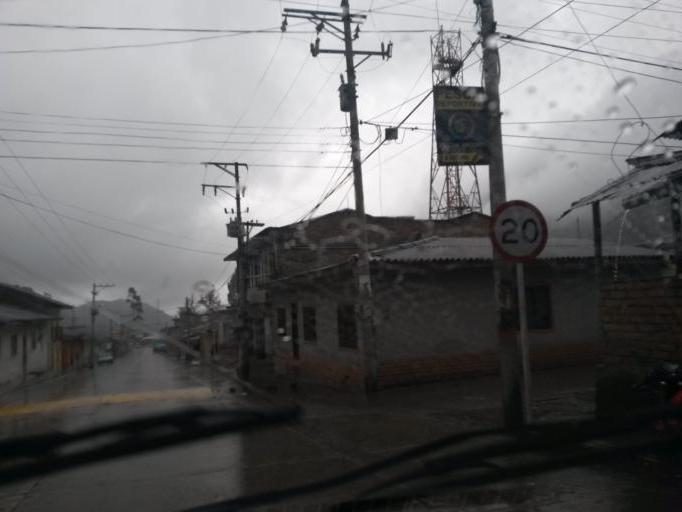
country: CO
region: Cauca
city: Paispamba
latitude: 2.3432
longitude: -76.4965
